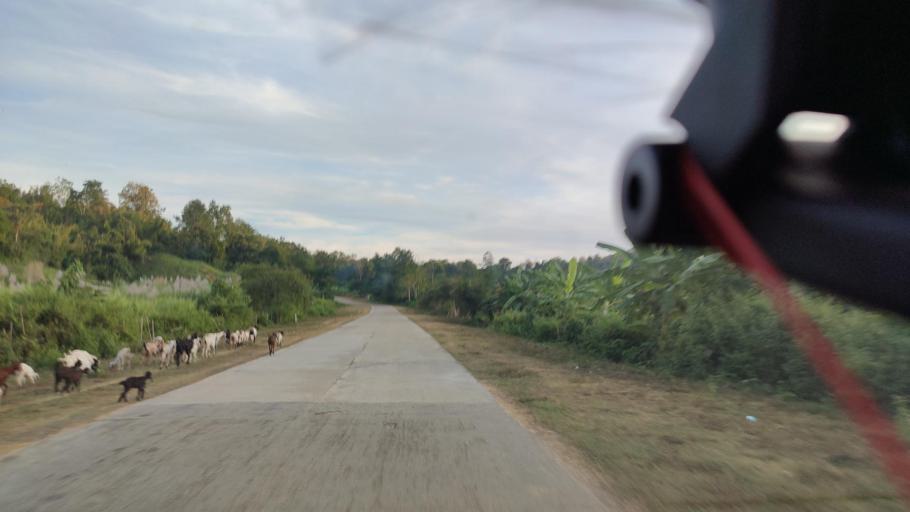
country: MM
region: Mandalay
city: Nay Pyi Taw
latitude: 19.9318
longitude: 95.9794
